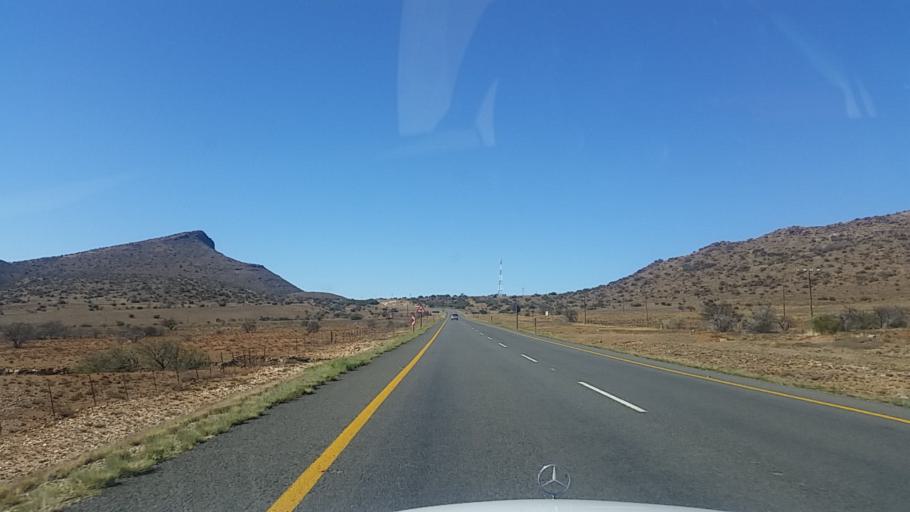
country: ZA
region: Eastern Cape
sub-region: Cacadu District Municipality
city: Graaff-Reinet
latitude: -32.1005
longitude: 24.6054
